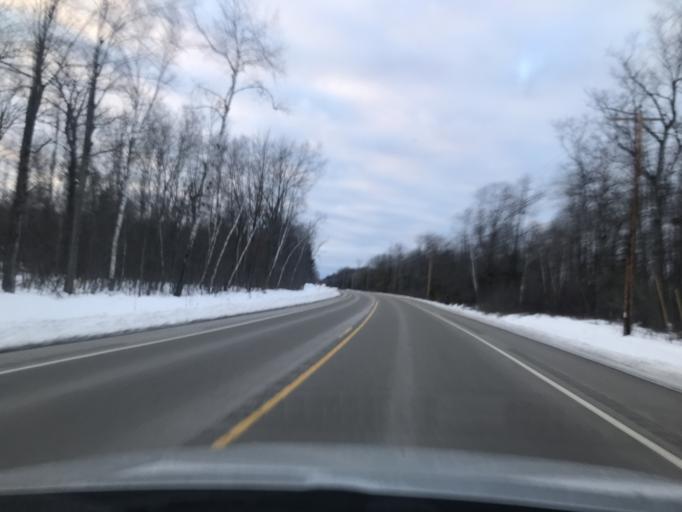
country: US
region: Wisconsin
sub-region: Marinette County
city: Marinette
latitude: 45.1526
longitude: -87.7067
